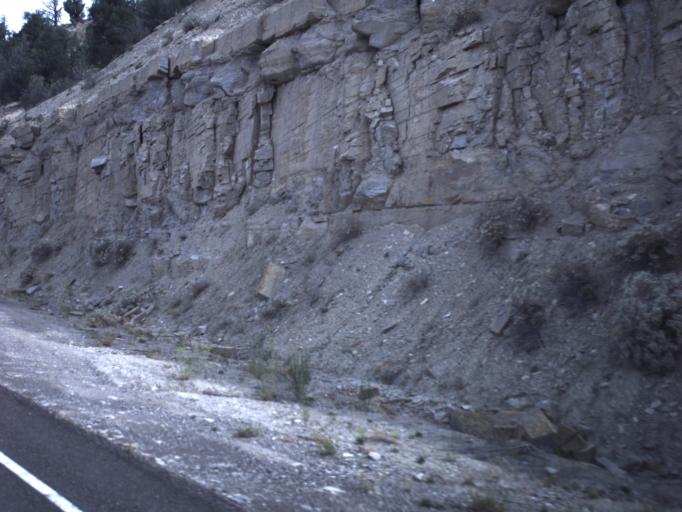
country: US
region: Utah
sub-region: Kane County
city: Kanab
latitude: 37.2256
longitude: -112.6838
